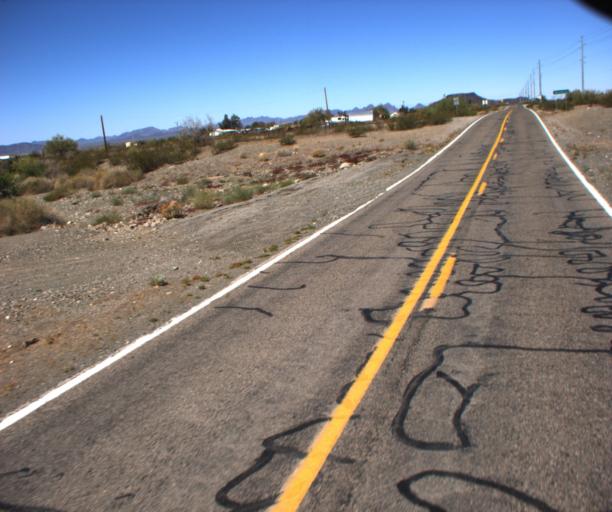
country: US
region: Arizona
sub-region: La Paz County
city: Salome
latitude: 33.7429
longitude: -113.7476
